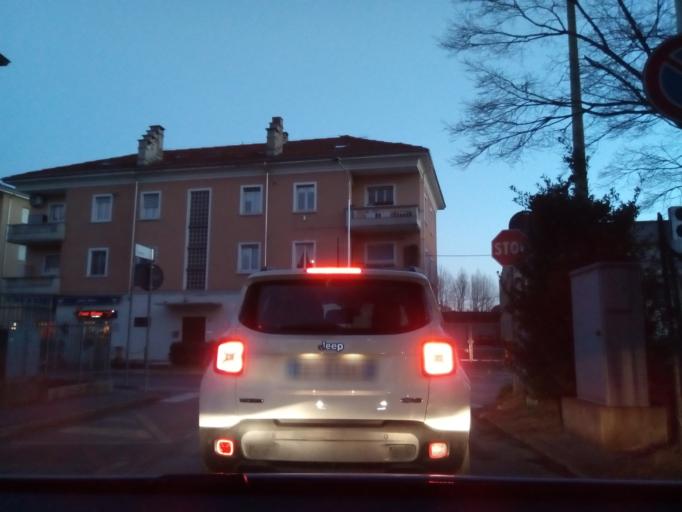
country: IT
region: Piedmont
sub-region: Provincia di Torino
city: Ivrea
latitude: 45.4714
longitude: 7.8900
